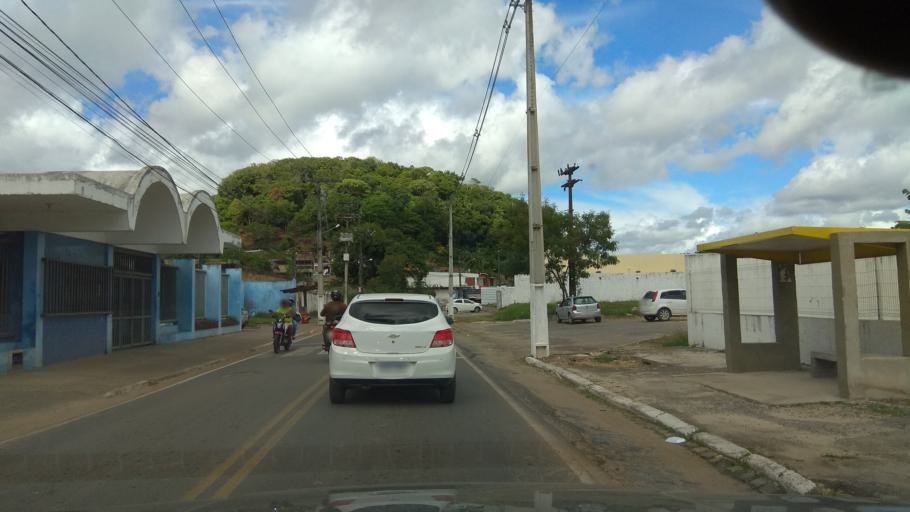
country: BR
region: Bahia
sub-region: Ilheus
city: Ilheus
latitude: -14.7886
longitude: -39.0606
